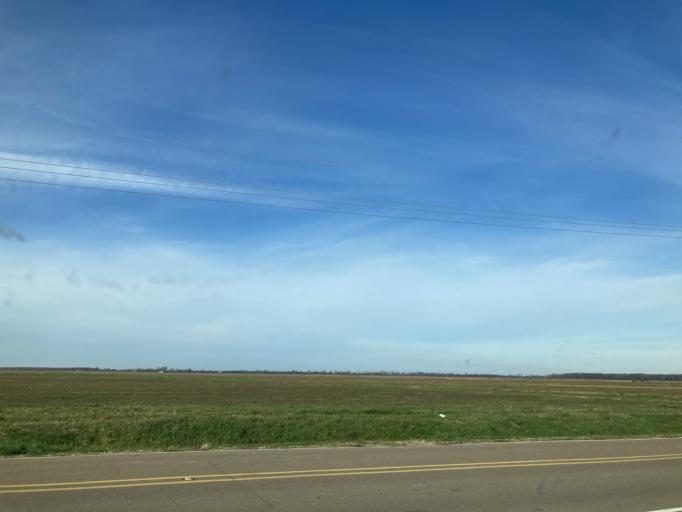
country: US
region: Mississippi
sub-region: Humphreys County
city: Belzoni
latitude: 32.9886
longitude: -90.5900
